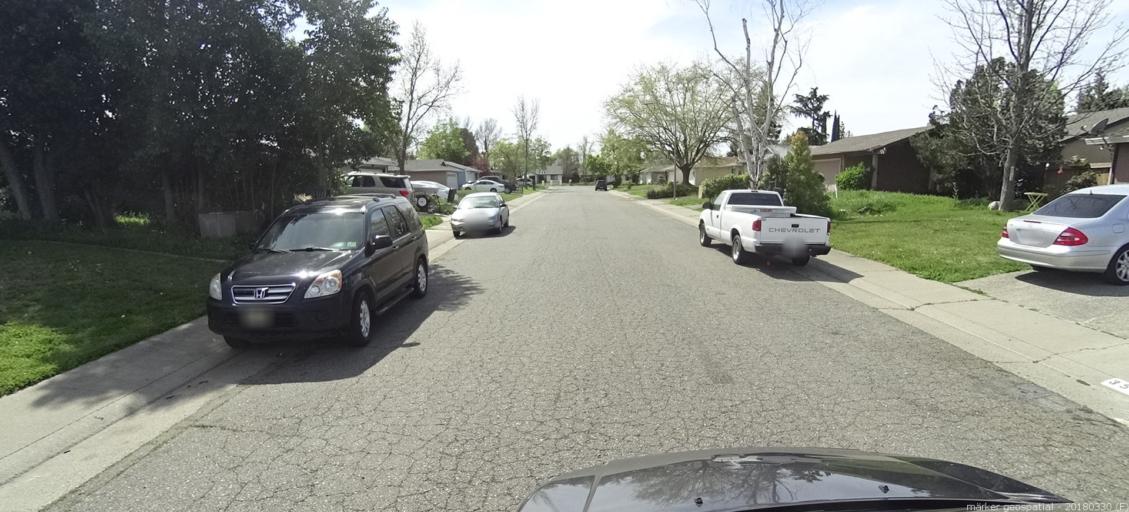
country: US
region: California
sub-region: Sacramento County
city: Rosemont
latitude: 38.5464
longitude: -121.3673
